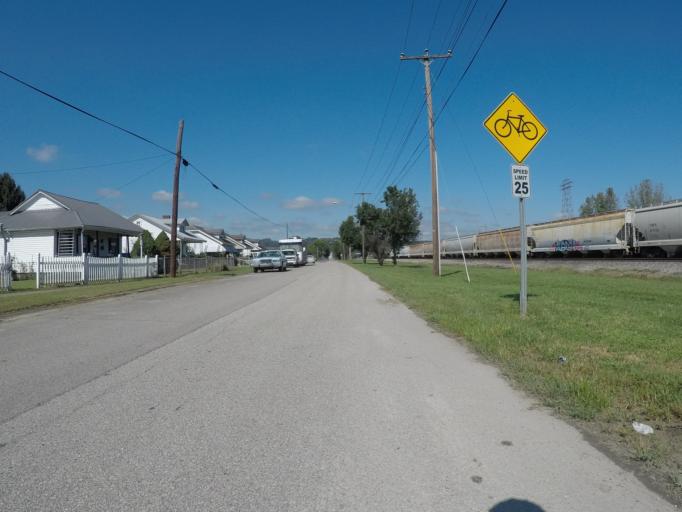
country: US
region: West Virginia
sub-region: Wayne County
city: Kenova
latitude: 38.4041
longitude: -82.5804
